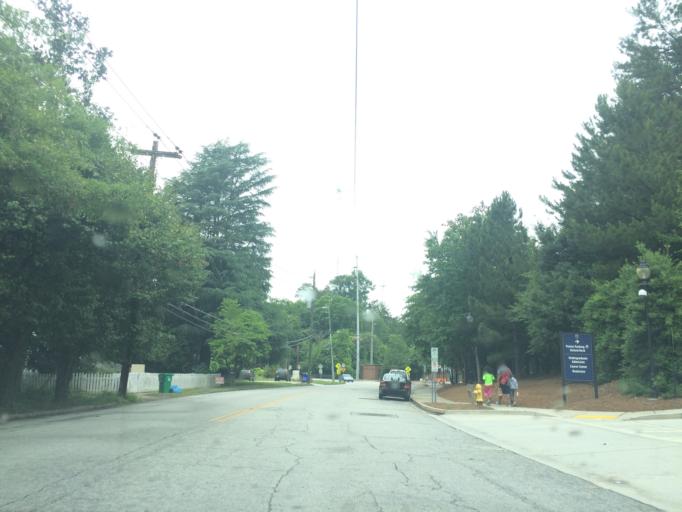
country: US
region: Georgia
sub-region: DeKalb County
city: Druid Hills
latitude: 33.7896
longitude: -84.3275
